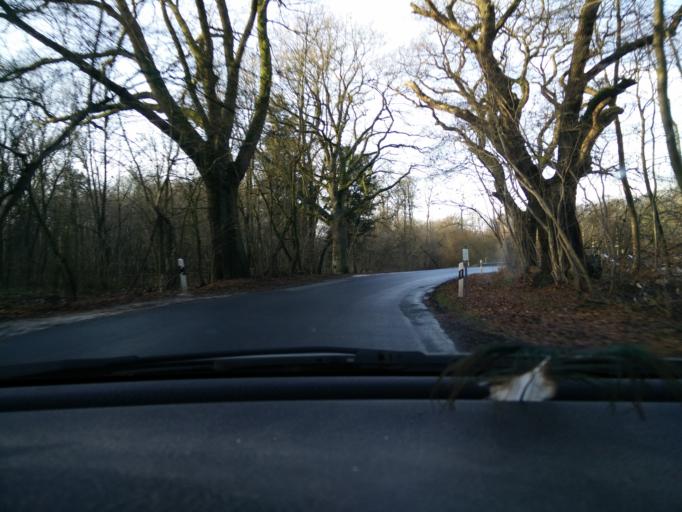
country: DE
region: Hamburg
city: Duvenstedt
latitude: 53.7201
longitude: 10.1178
